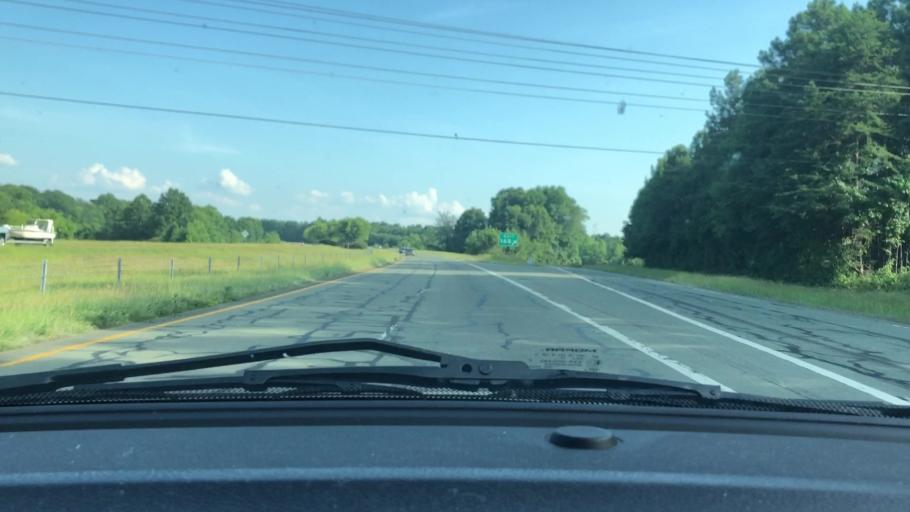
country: US
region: North Carolina
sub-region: Chatham County
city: Siler City
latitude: 35.6975
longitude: -79.4288
